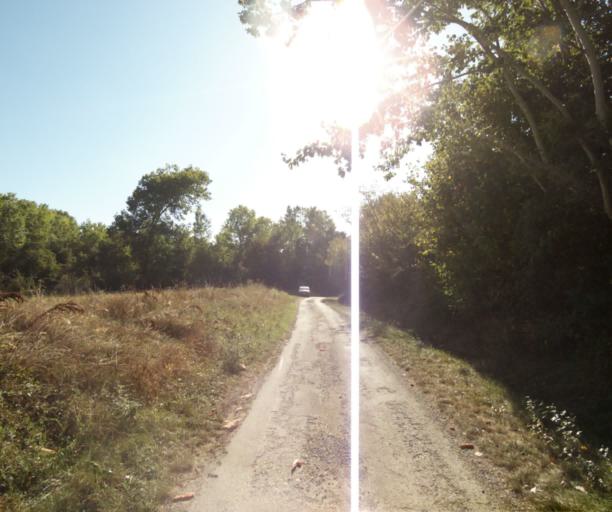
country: FR
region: Midi-Pyrenees
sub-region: Departement du Tarn-et-Garonne
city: Verdun-sur-Garonne
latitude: 43.8644
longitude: 1.2212
